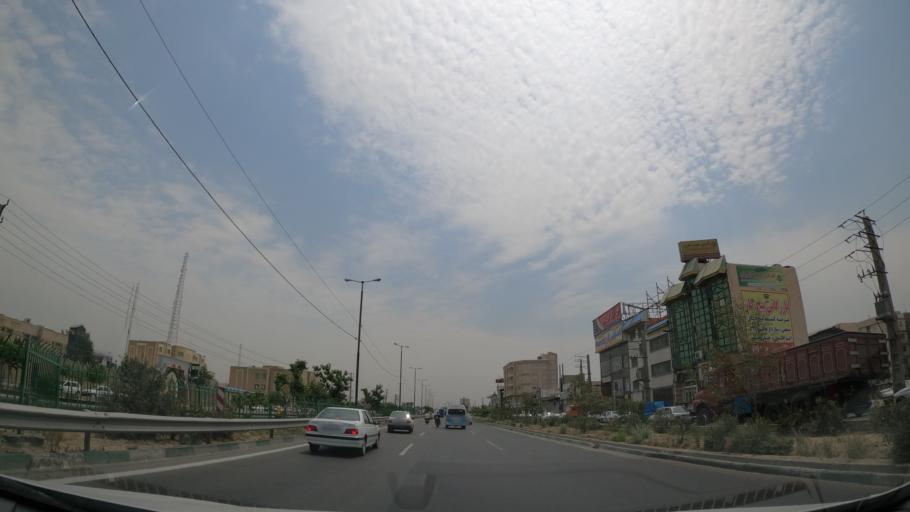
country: IR
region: Tehran
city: Eslamshahr
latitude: 35.6769
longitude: 51.2729
